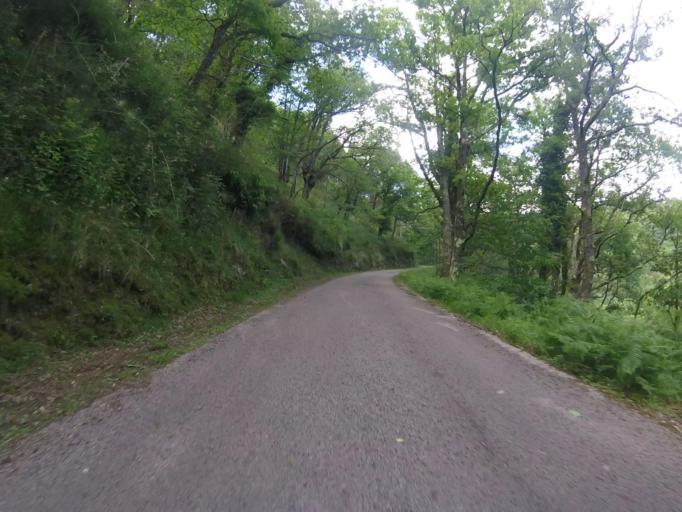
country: ES
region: Navarre
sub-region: Provincia de Navarra
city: Goizueta
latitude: 43.2198
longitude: -1.8075
